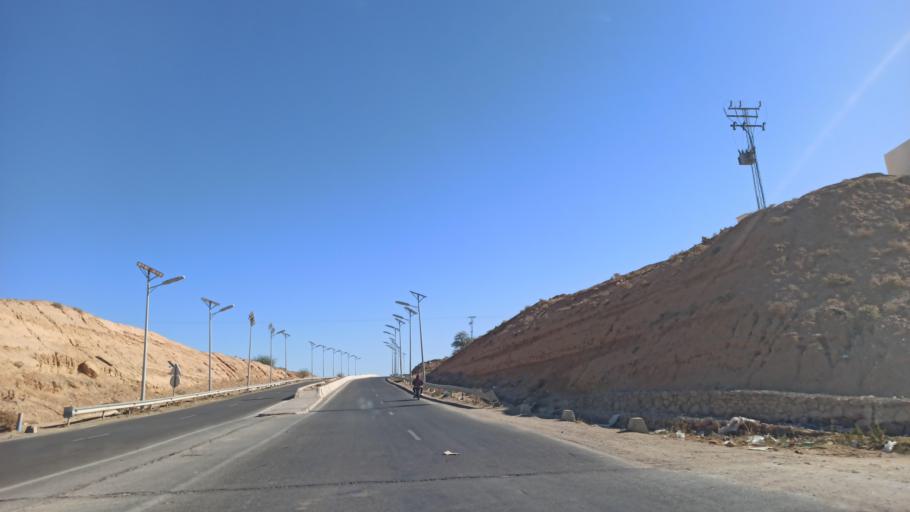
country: TN
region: Gafsa
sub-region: Gafsa Municipality
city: Gafsa
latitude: 34.4332
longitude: 8.8090
